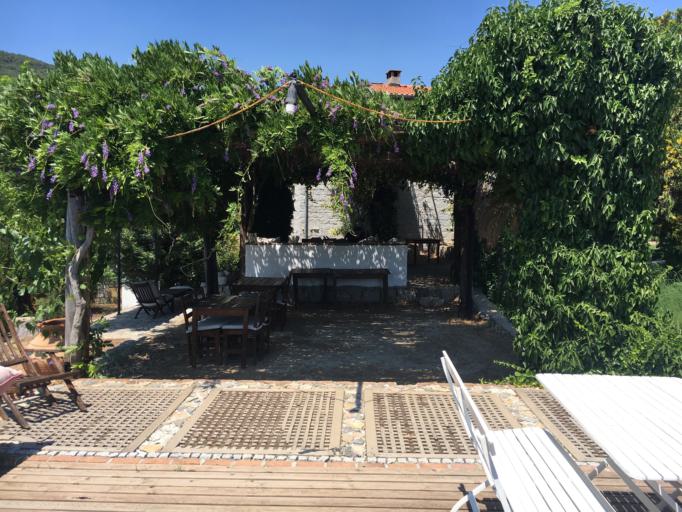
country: TR
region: Balikesir
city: Altinoluk
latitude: 39.5989
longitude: 26.8622
